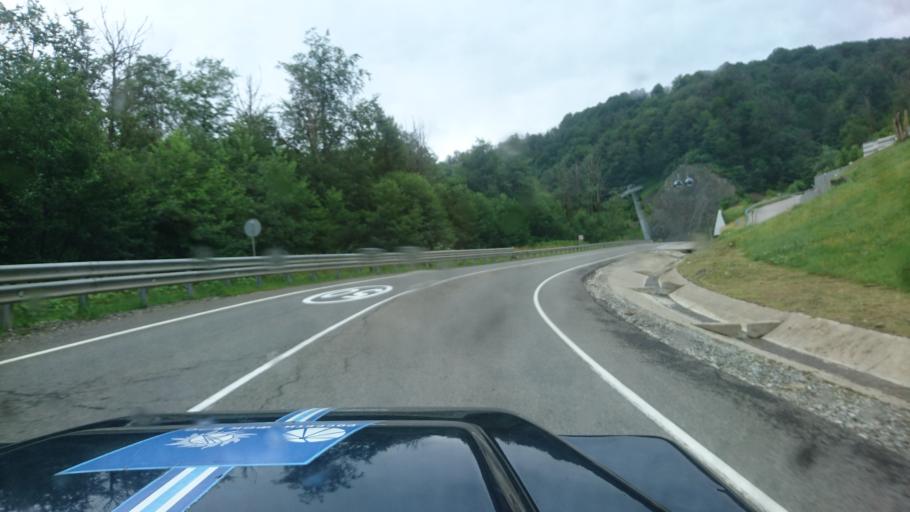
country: RU
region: Krasnodarskiy
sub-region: Sochi City
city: Krasnaya Polyana
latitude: 43.6681
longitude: 40.2910
